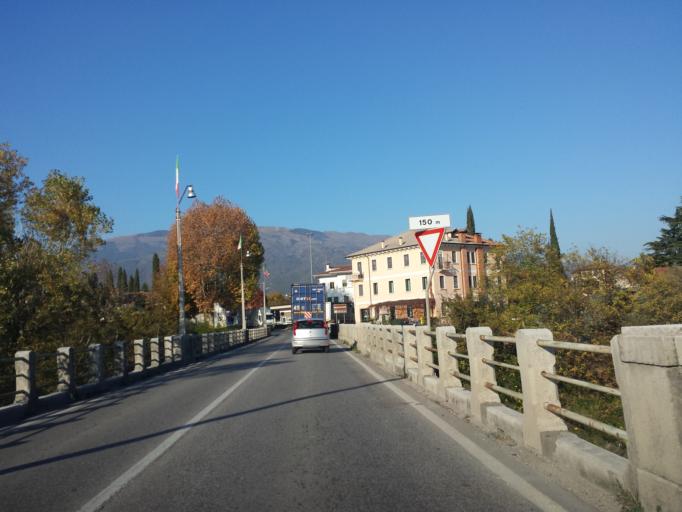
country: IT
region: Veneto
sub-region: Provincia di Treviso
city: Bigolino
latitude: 45.8596
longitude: 12.0248
